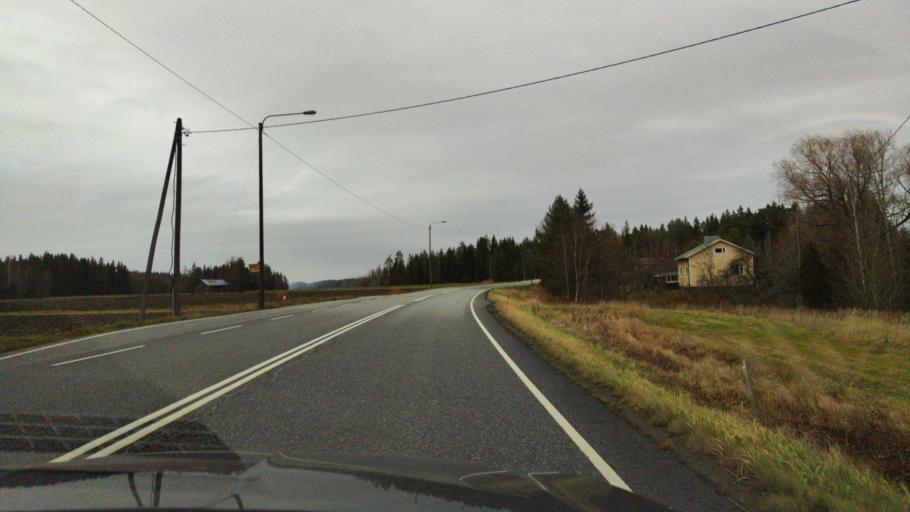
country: FI
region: Varsinais-Suomi
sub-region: Turku
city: Vahto
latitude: 60.6379
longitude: 22.4196
